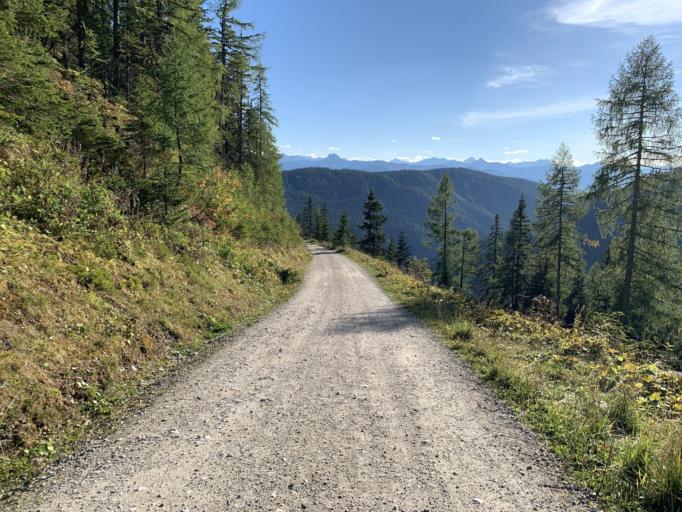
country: AT
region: Styria
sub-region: Politischer Bezirk Liezen
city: Schladming
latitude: 47.4404
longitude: 13.6155
